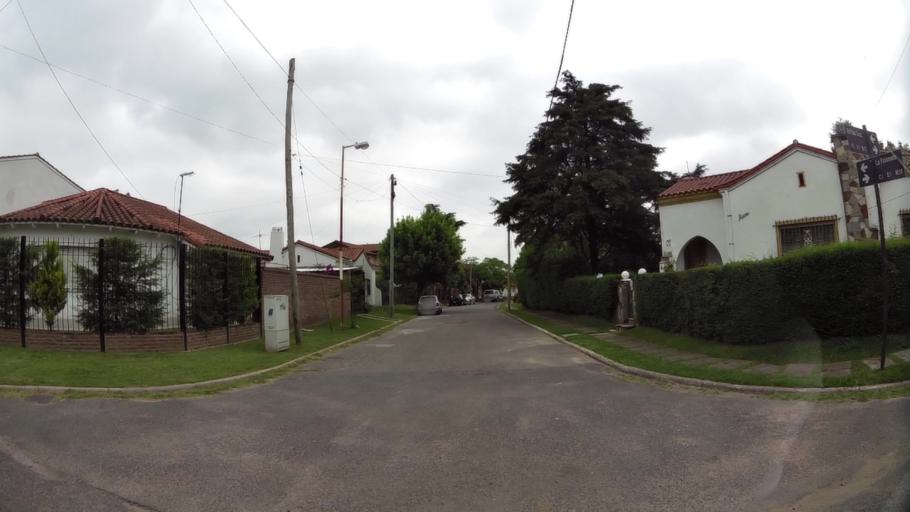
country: AR
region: Buenos Aires
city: San Justo
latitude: -34.7355
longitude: -58.5246
